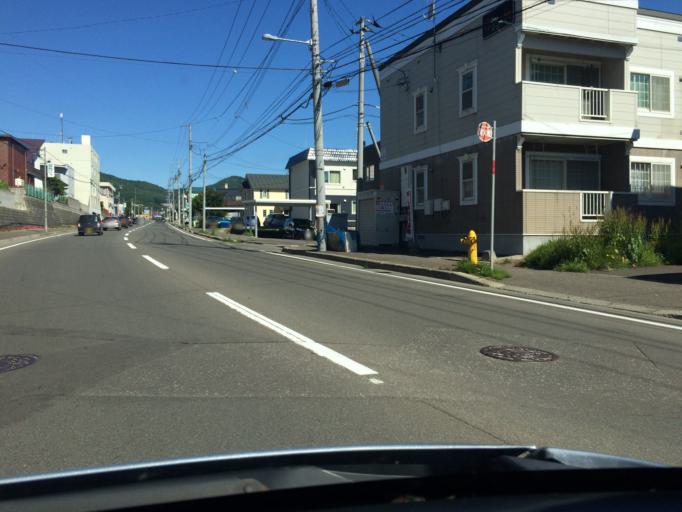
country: JP
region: Hokkaido
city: Sapporo
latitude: 43.0025
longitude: 141.3205
